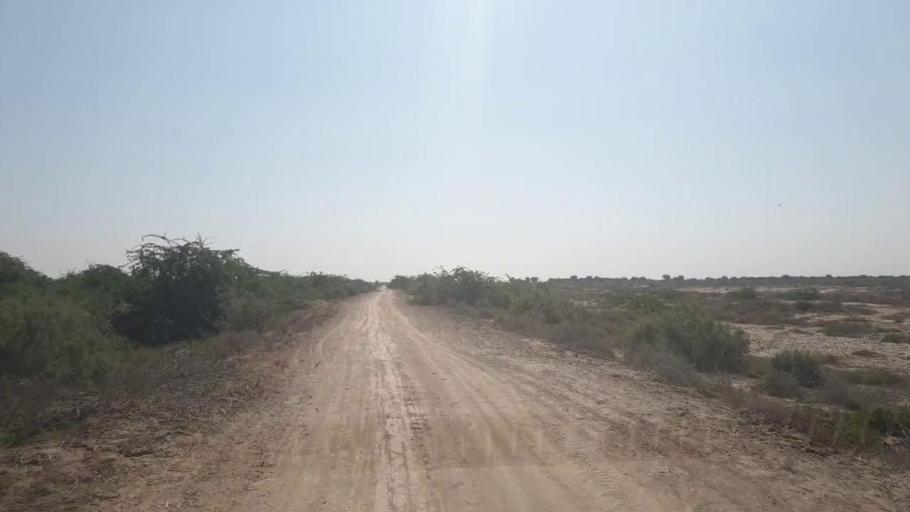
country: PK
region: Sindh
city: Tando Bago
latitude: 24.8843
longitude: 69.1644
